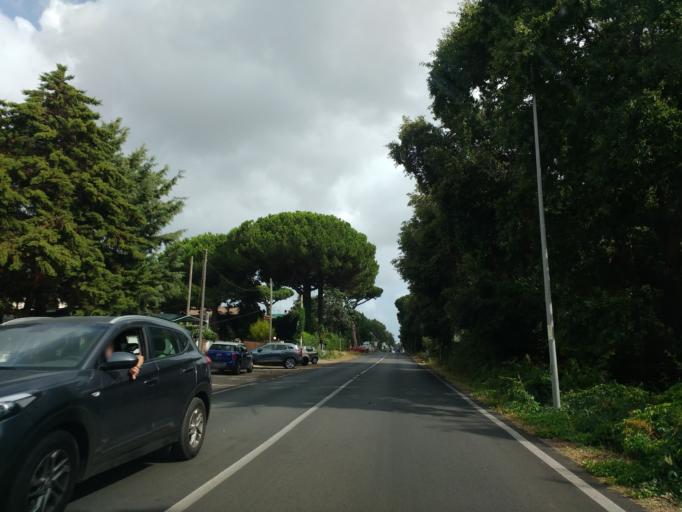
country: IT
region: Latium
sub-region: Citta metropolitana di Roma Capitale
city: Lavinio
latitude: 41.4898
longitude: 12.5971
